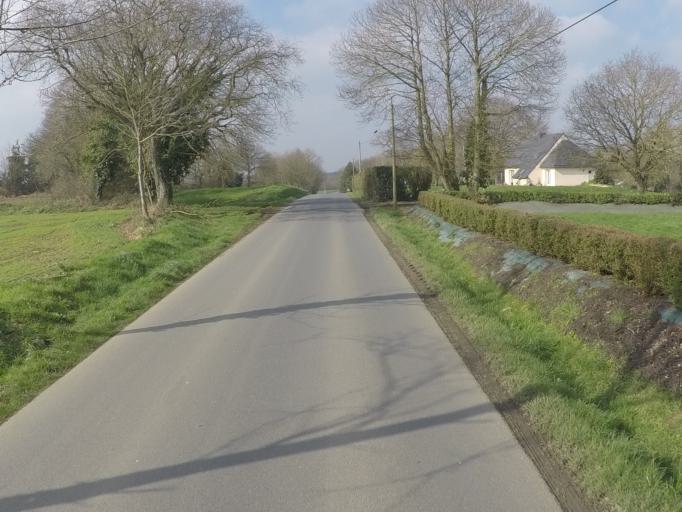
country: FR
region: Brittany
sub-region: Departement des Cotes-d'Armor
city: Goudelin
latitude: 48.6063
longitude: -3.0266
